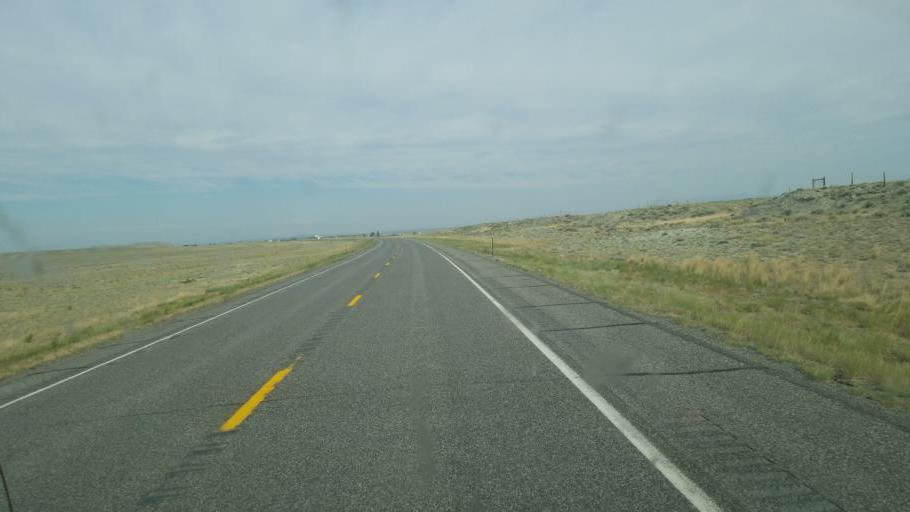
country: US
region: Wyoming
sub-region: Fremont County
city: Riverton
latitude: 43.2356
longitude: -108.0745
